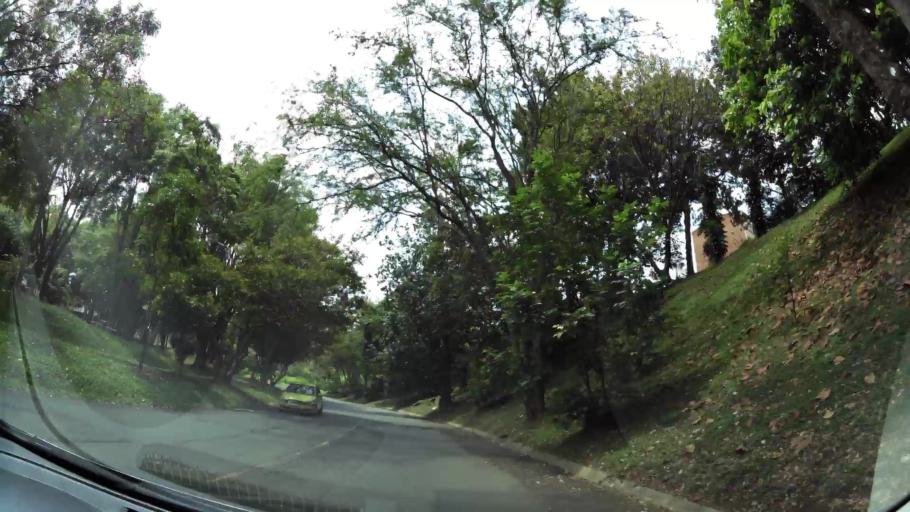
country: CO
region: Antioquia
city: Medellin
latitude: 6.2488
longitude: -75.6162
